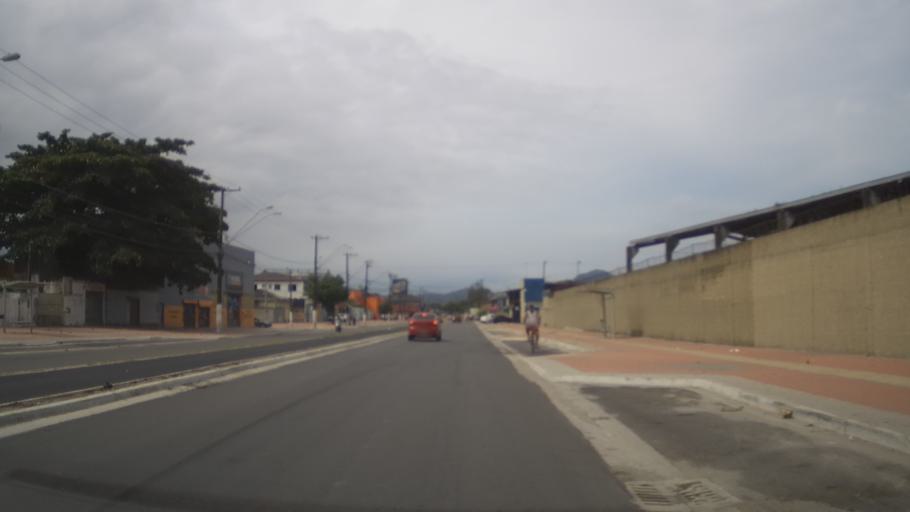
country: BR
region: Sao Paulo
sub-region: Praia Grande
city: Praia Grande
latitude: -24.0069
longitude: -46.4470
